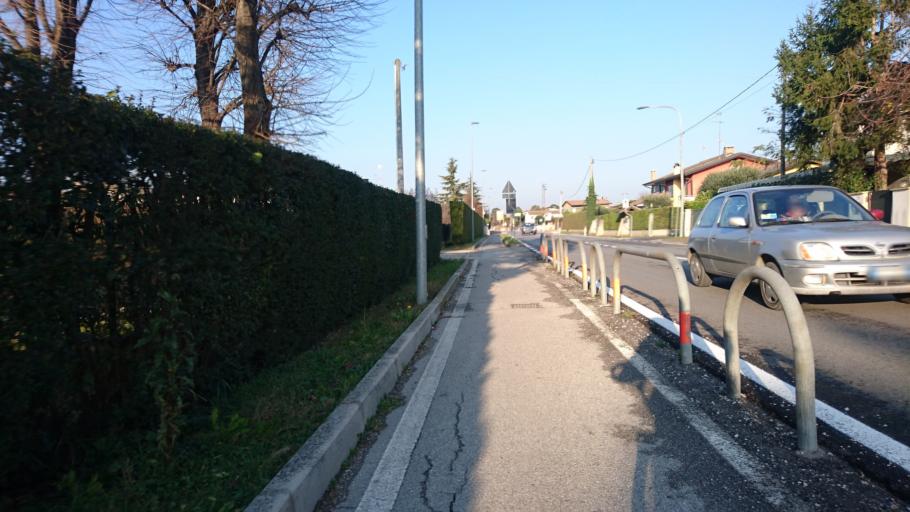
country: IT
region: Veneto
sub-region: Provincia di Padova
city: Polverara
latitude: 45.3226
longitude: 11.9638
